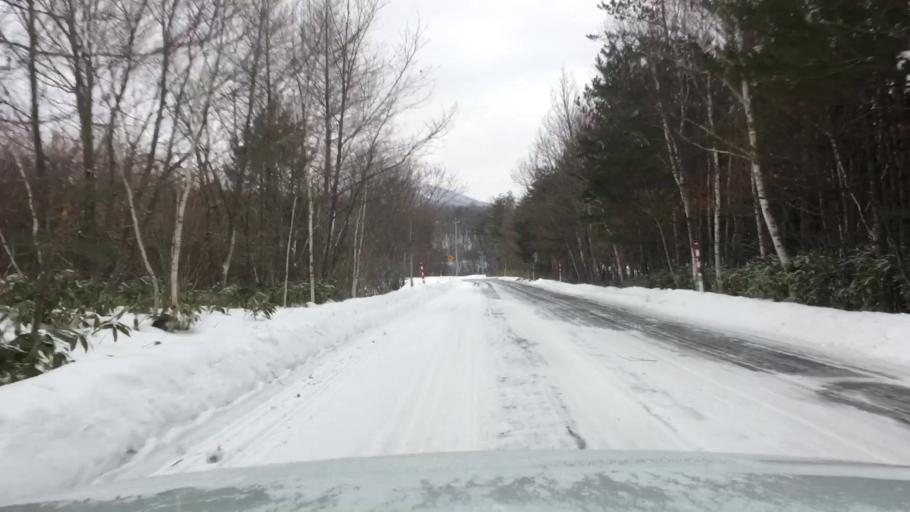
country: JP
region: Iwate
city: Shizukuishi
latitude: 39.9376
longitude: 141.0012
